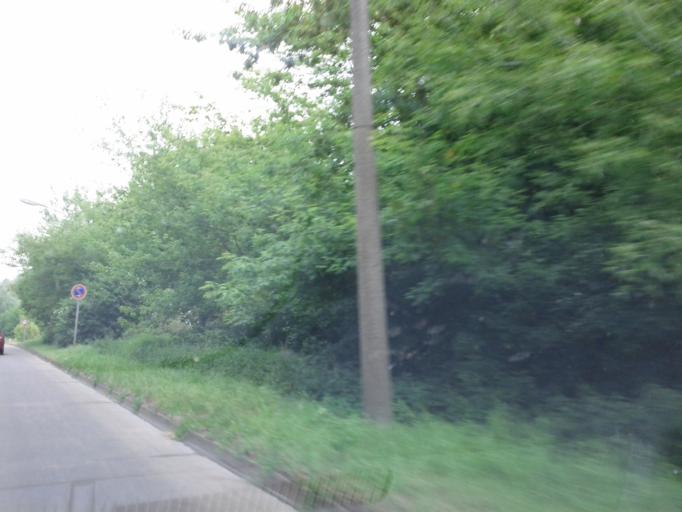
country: DE
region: Brandenburg
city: Ahrensfelde
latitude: 52.5640
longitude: 13.5798
